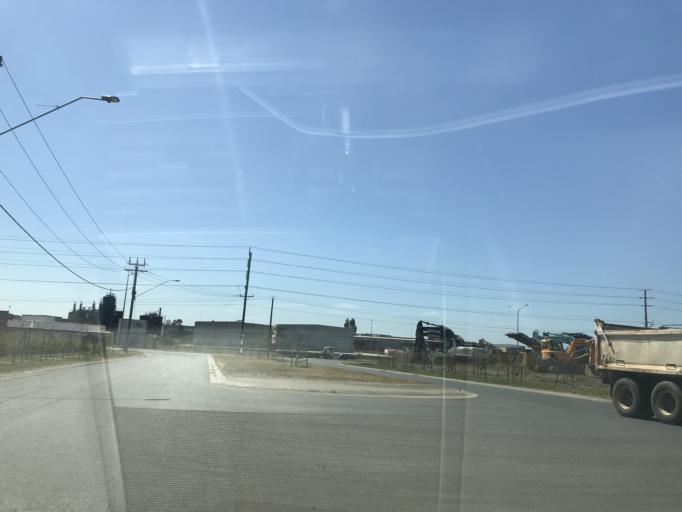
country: AU
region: Victoria
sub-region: Wyndham
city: Truganina
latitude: -37.8280
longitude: 144.7704
